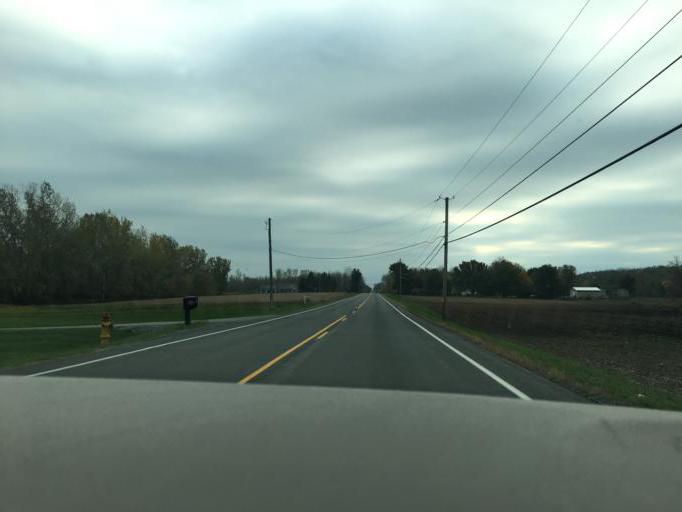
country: US
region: New York
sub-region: Wayne County
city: Macedon
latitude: 43.0176
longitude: -77.3239
